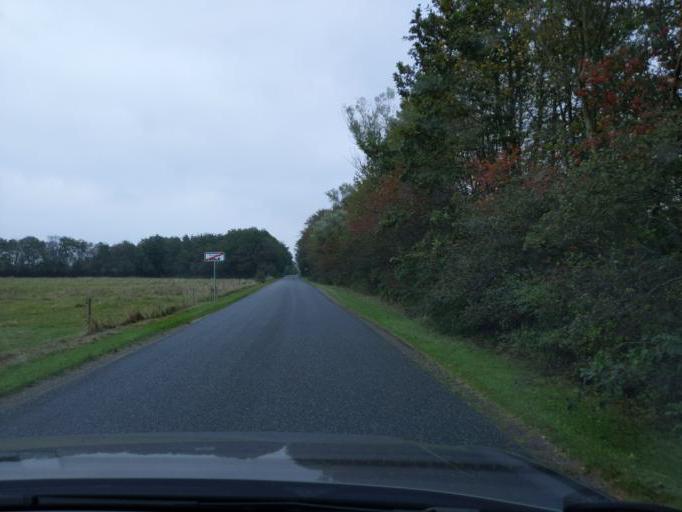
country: DK
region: Central Jutland
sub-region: Viborg Kommune
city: Karup
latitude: 56.3661
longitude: 9.2185
